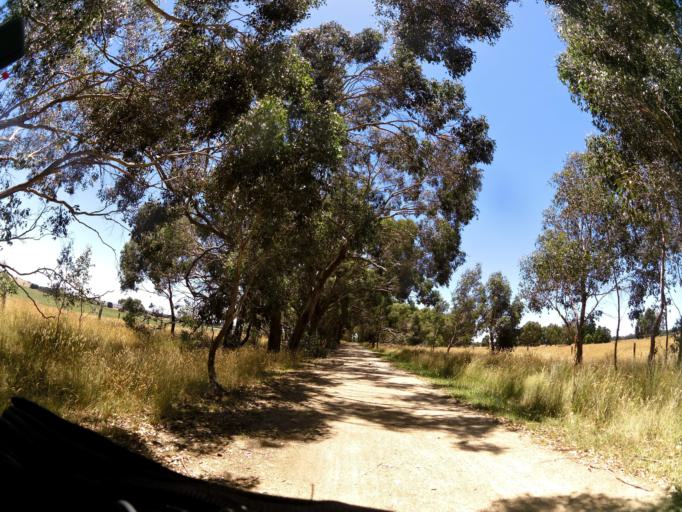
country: AU
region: Victoria
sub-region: Ballarat North
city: Delacombe
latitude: -37.5669
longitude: 143.7318
